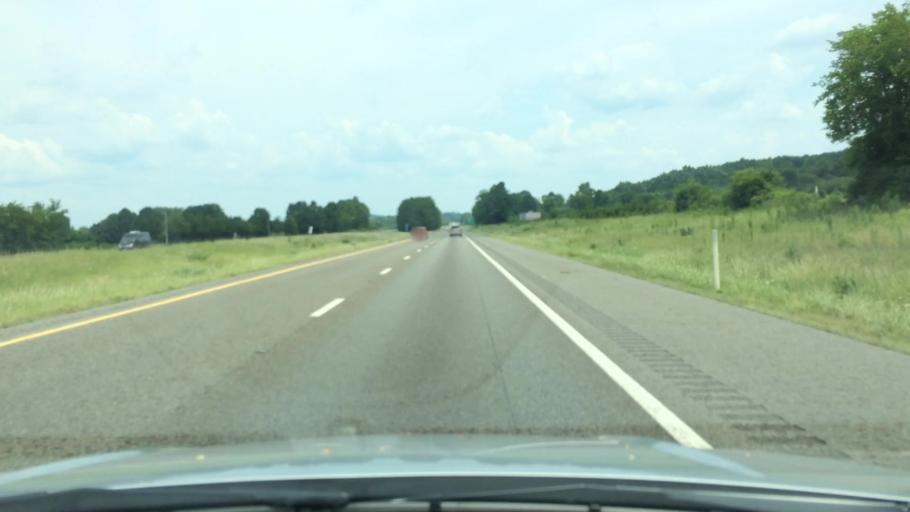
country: US
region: Tennessee
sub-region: Marshall County
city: Cornersville
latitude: 35.4399
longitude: -86.8817
